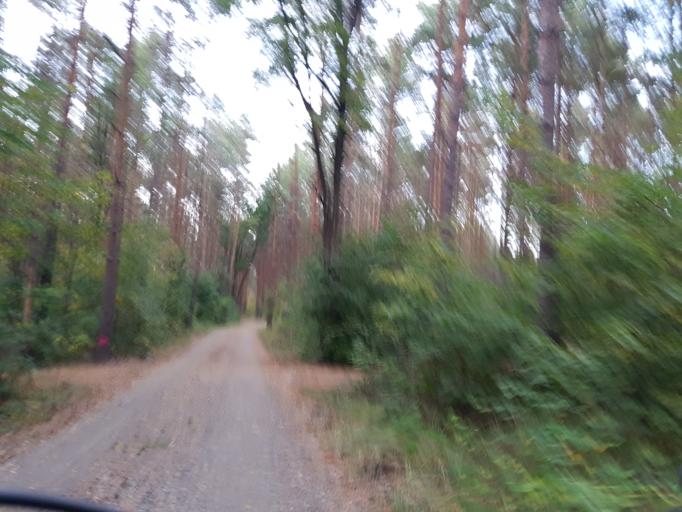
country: DE
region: Brandenburg
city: Trobitz
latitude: 51.5773
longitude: 13.4590
